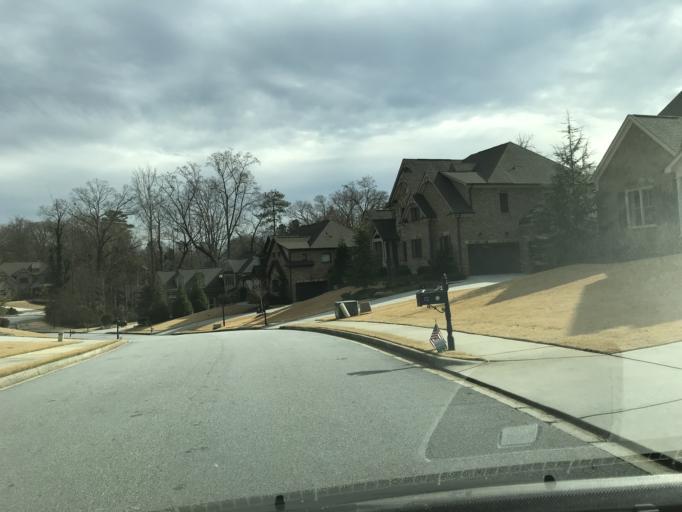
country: US
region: Georgia
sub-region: DeKalb County
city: North Atlanta
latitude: 33.8789
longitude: -84.3470
